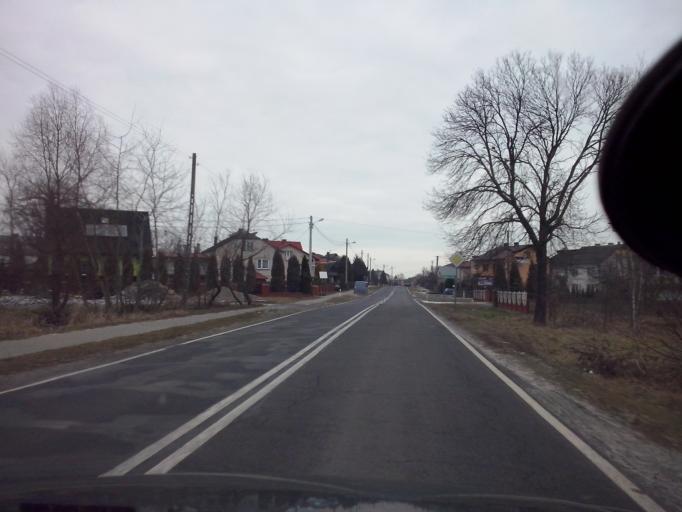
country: PL
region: Lublin Voivodeship
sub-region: Powiat bilgorajski
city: Biszcza
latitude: 50.4940
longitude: 22.6357
